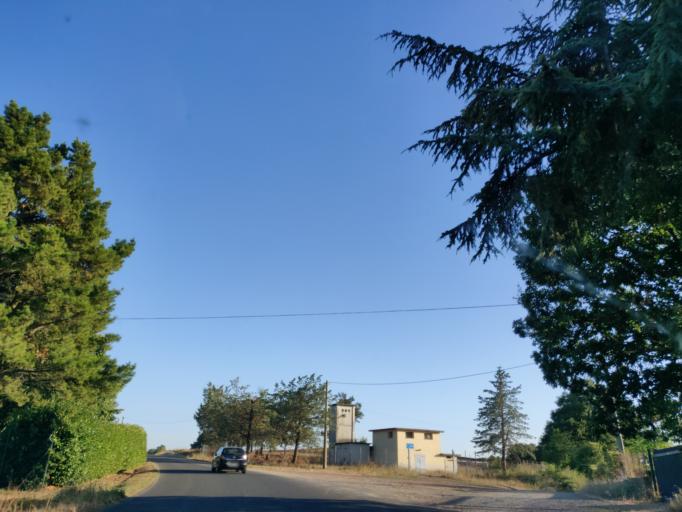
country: IT
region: Latium
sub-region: Provincia di Viterbo
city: Acquapendente
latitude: 42.7226
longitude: 11.8739
